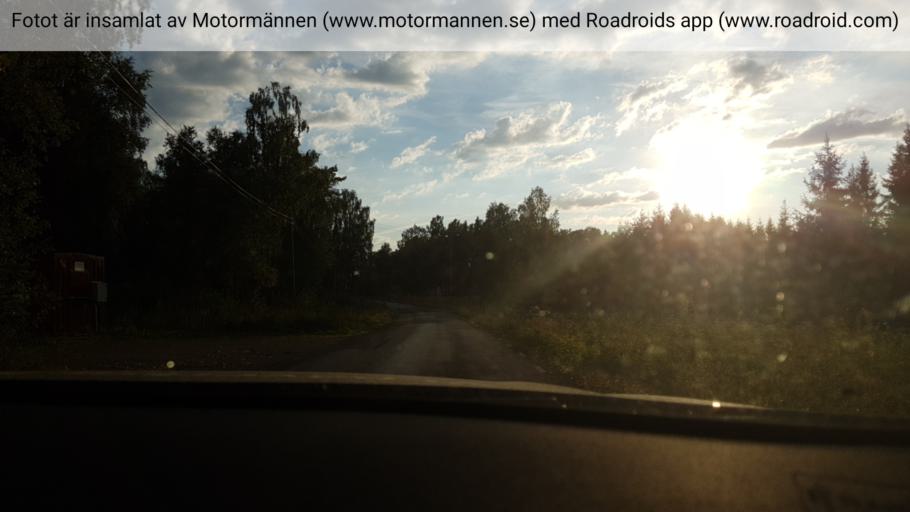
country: SE
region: Vaestra Goetaland
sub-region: Falkopings Kommun
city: Floby
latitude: 57.9934
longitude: 13.4472
